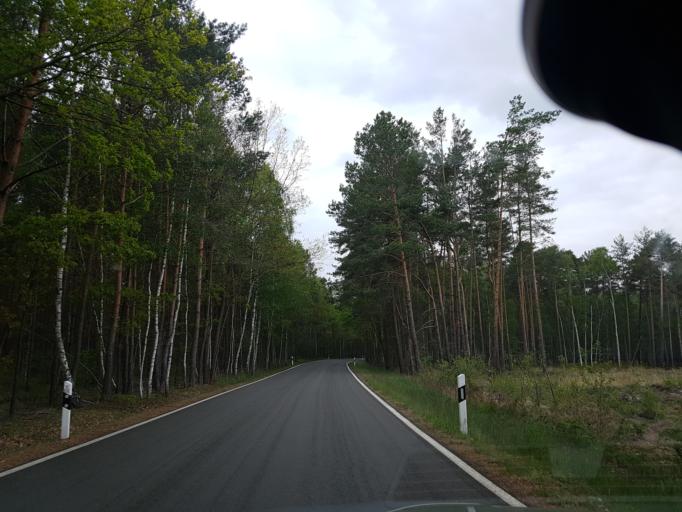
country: DE
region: Brandenburg
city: Crinitz
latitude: 51.7499
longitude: 13.7533
